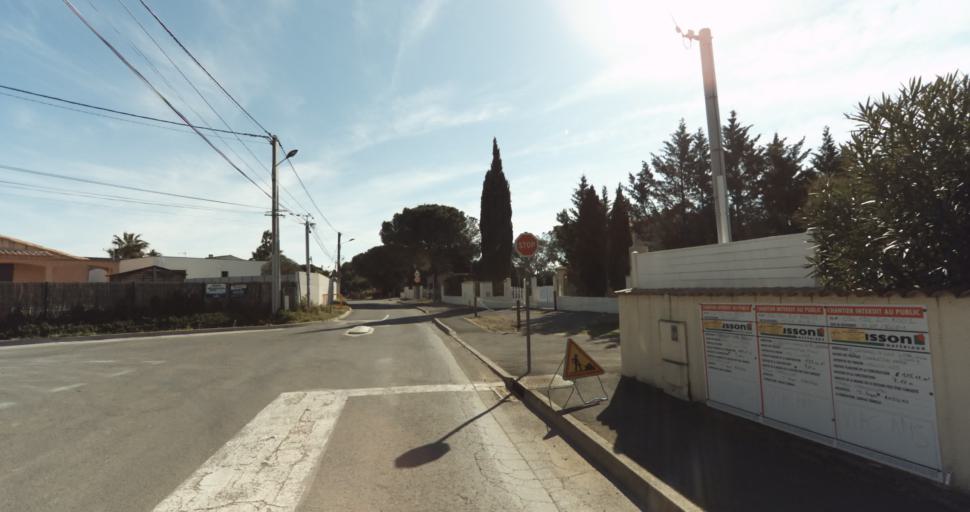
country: FR
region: Languedoc-Roussillon
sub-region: Departement de l'Herault
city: Marseillan
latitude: 43.3343
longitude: 3.5198
